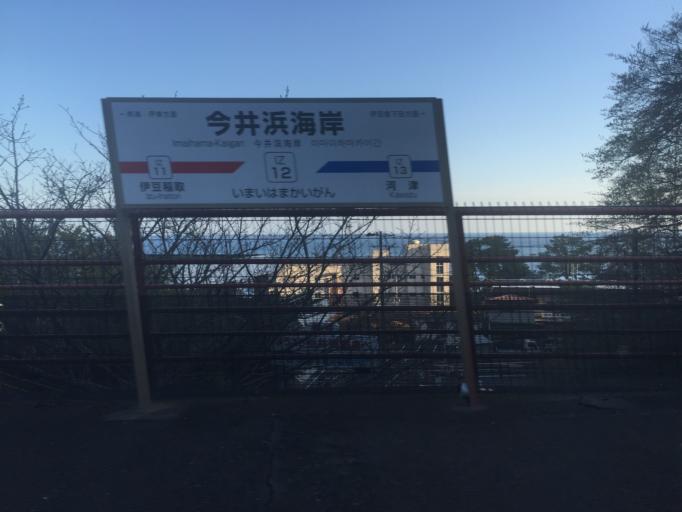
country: JP
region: Shizuoka
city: Shimoda
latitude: 34.7536
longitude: 139.0043
